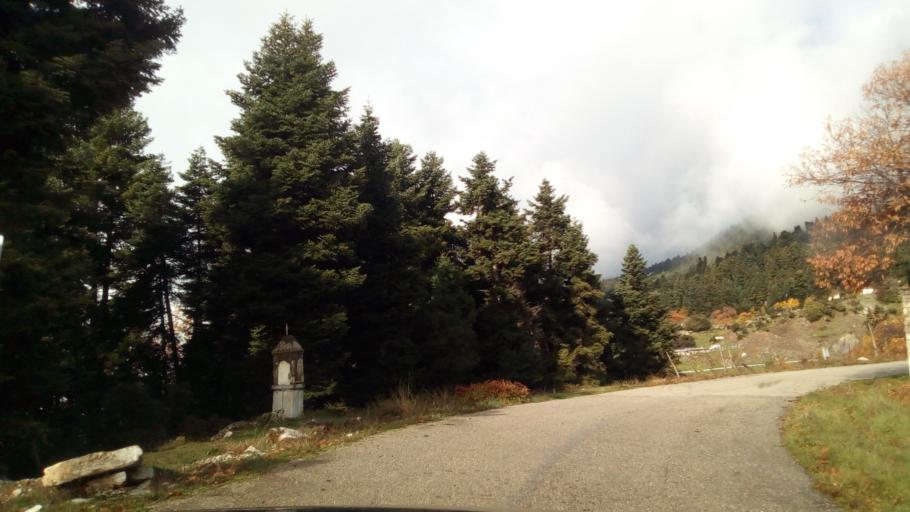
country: GR
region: West Greece
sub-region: Nomos Aitolias kai Akarnanias
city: Nafpaktos
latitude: 38.5655
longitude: 21.9247
